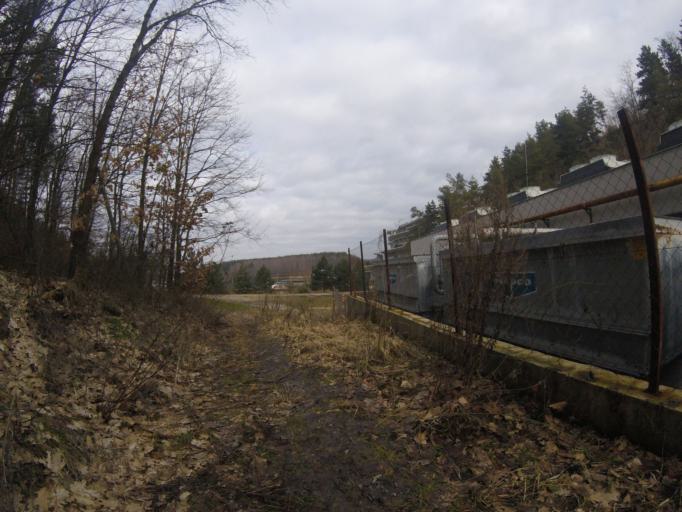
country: HU
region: Heves
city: Egerszalok
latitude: 47.8526
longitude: 20.3358
